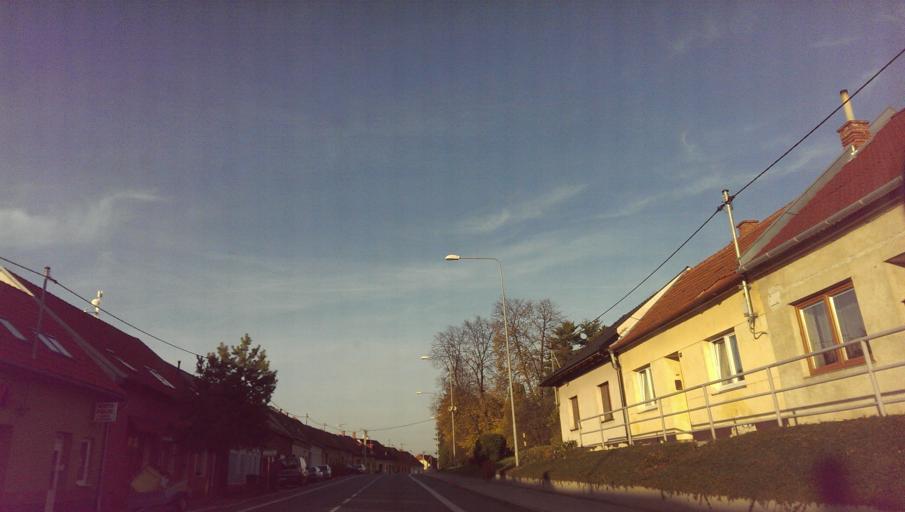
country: CZ
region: Zlin
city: Kunovice
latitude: 49.0365
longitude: 17.4615
